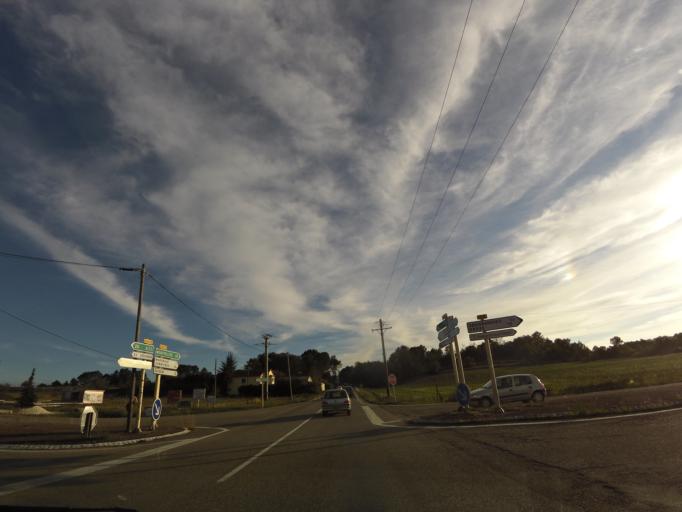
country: FR
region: Languedoc-Roussillon
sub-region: Departement du Gard
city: Ledignan
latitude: 43.9572
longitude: 4.0992
